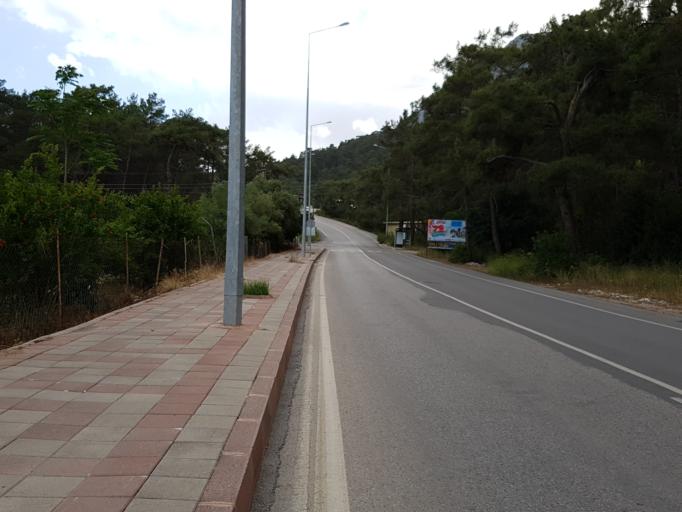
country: TR
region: Antalya
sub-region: Kemer
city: Goeynuek
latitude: 36.6449
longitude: 30.5485
